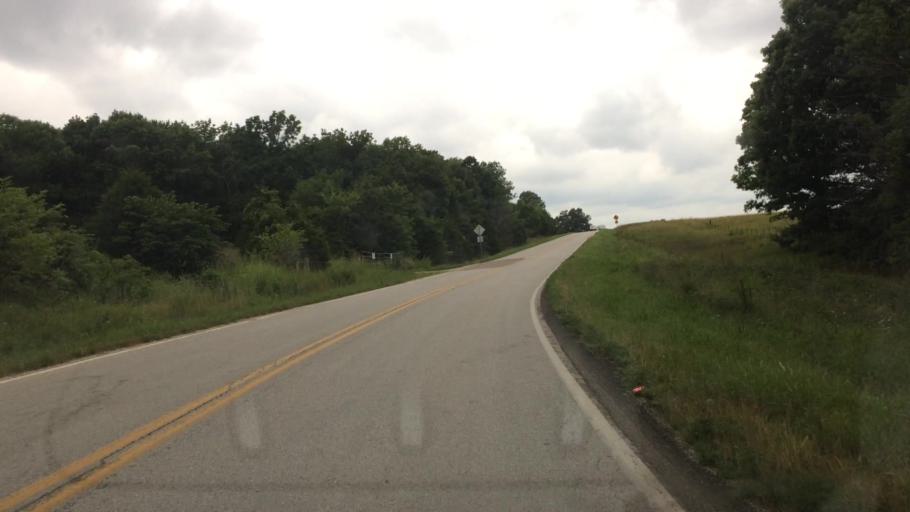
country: US
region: Missouri
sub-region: Webster County
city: Marshfield
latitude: 37.3035
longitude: -93.0029
